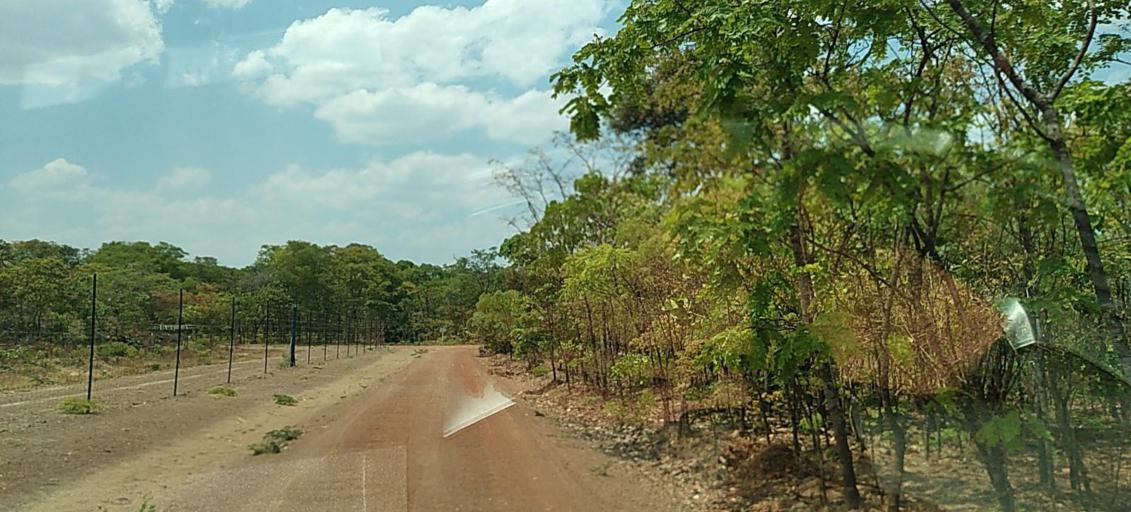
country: ZM
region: Copperbelt
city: Chililabombwe
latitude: -12.5157
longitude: 27.6272
